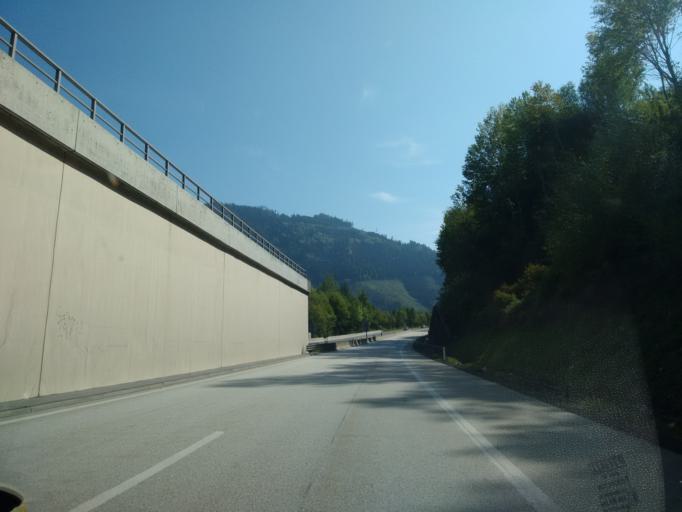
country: AT
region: Styria
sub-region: Politischer Bezirk Bruck-Muerzzuschlag
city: Oberaich
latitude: 47.4066
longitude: 15.1969
